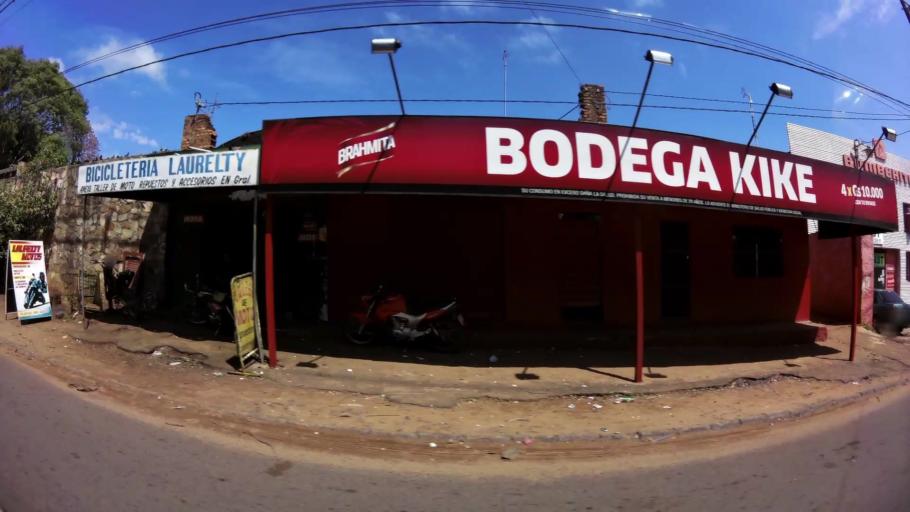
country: PY
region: Central
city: San Lorenzo
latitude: -25.3132
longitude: -57.5068
